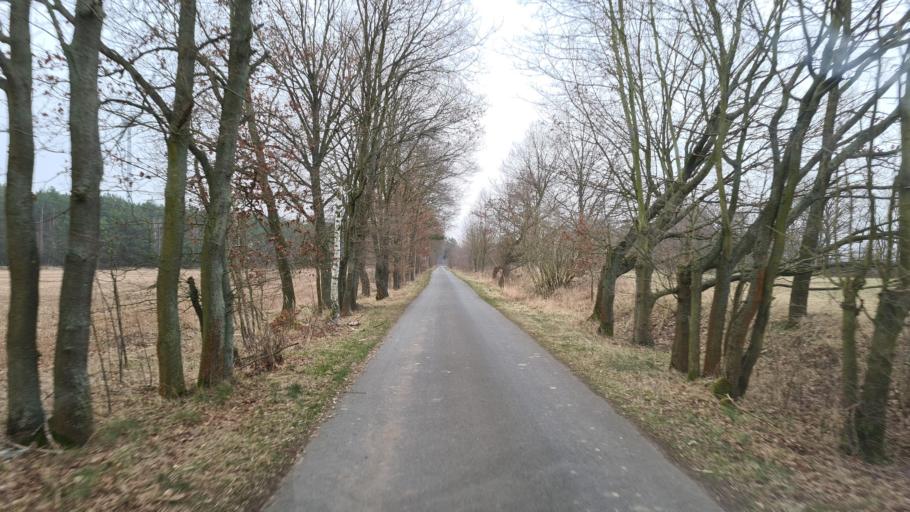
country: DE
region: Brandenburg
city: Herzberg
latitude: 51.6366
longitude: 13.2034
